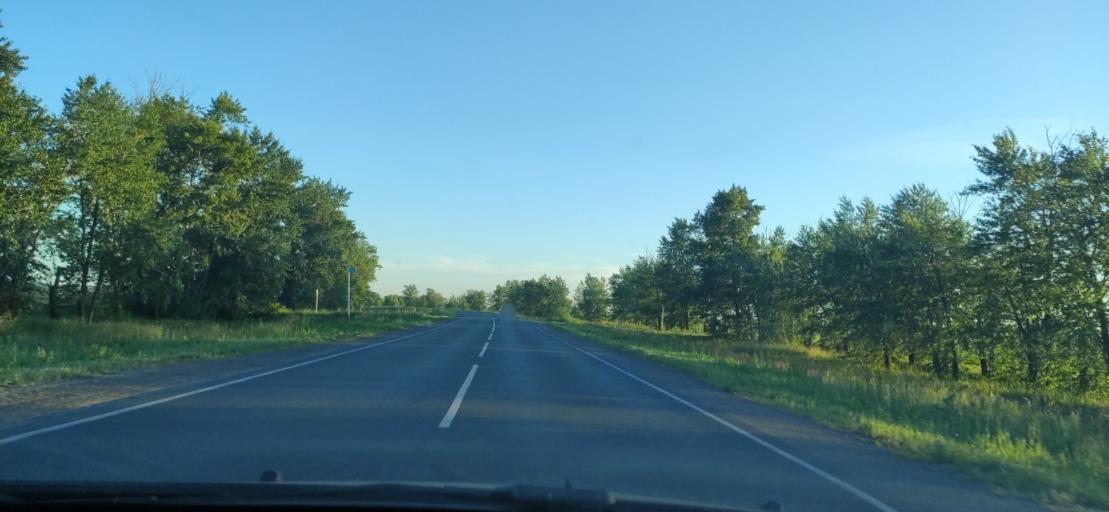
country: RU
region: Ulyanovsk
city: Cherdakly
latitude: 54.3988
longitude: 48.8584
